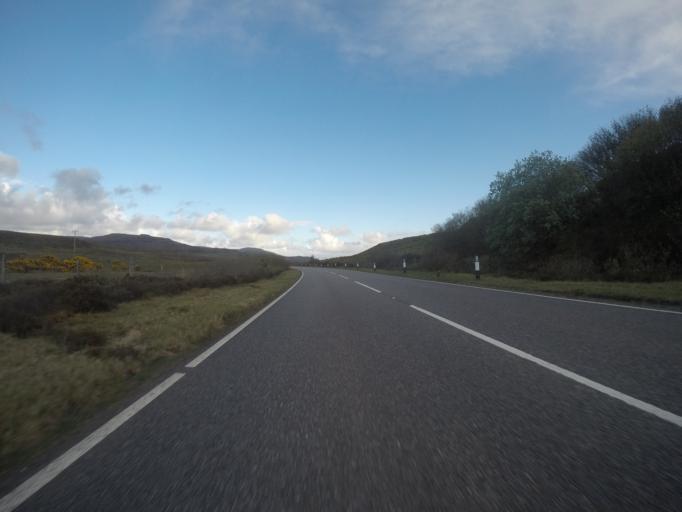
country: GB
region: Scotland
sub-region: Highland
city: Isle of Skye
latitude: 57.5060
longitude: -6.3348
